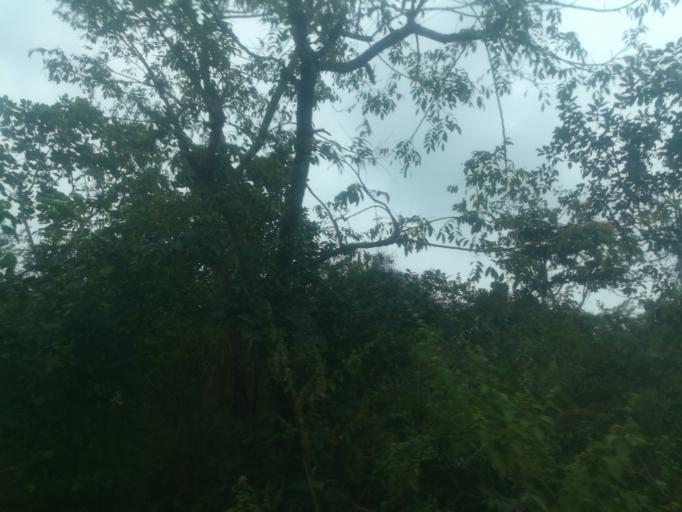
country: NG
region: Ogun
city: Itori
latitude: 7.1026
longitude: 3.1503
